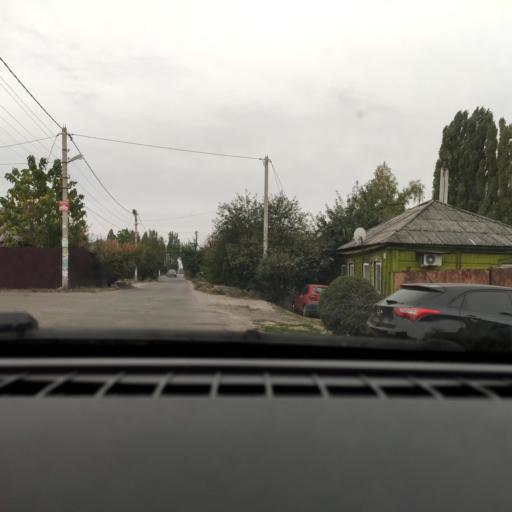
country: RU
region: Voronezj
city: Voronezh
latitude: 51.6705
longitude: 39.2637
